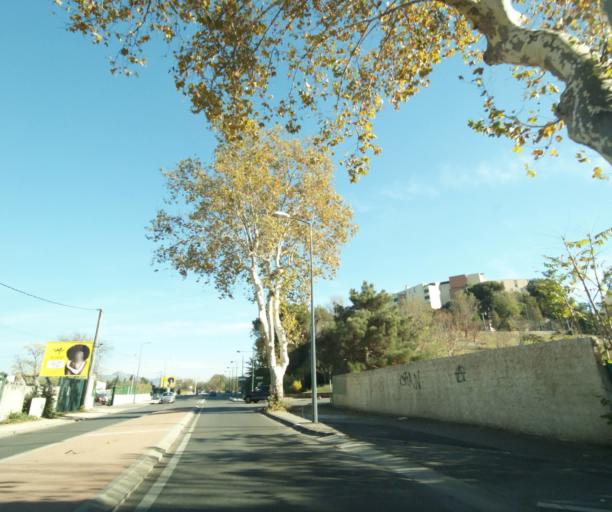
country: FR
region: Provence-Alpes-Cote d'Azur
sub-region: Departement des Bouches-du-Rhone
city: La Penne-sur-Huveaune
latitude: 43.2831
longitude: 5.5048
